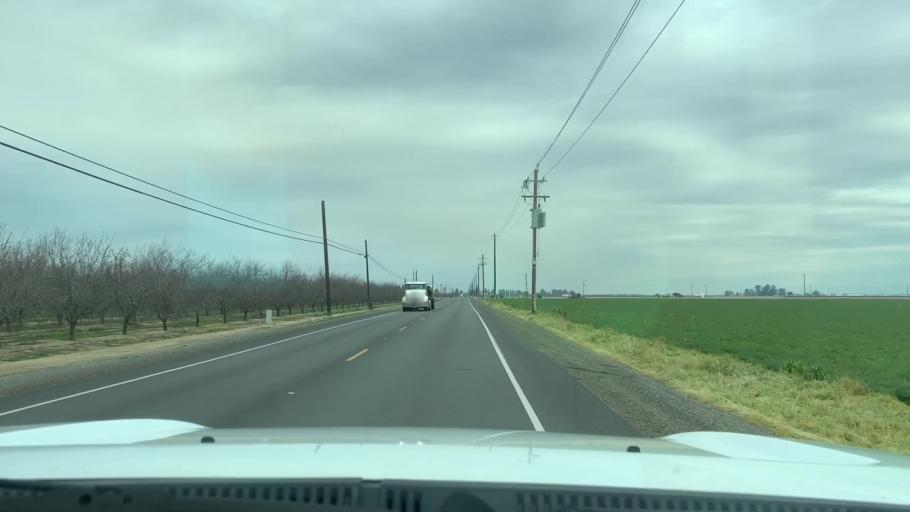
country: US
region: California
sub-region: Kern County
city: Shafter
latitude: 35.4062
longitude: -119.2519
